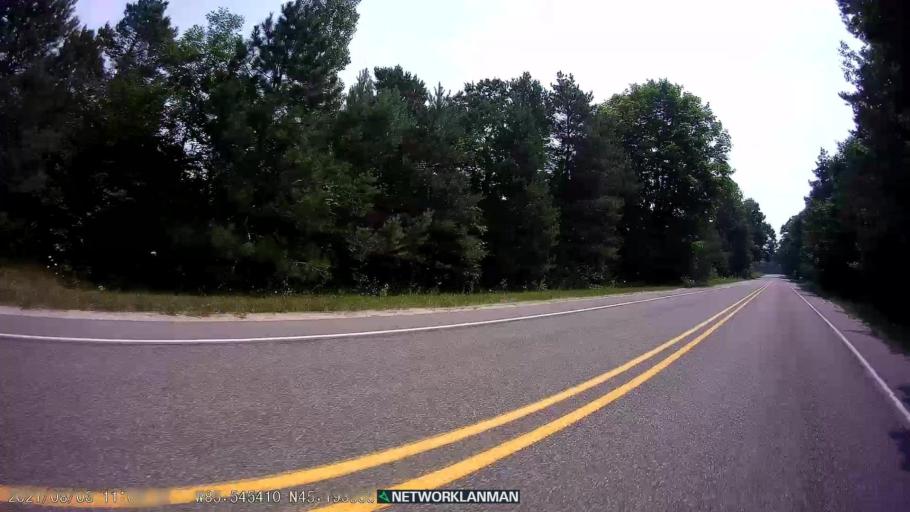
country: US
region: Michigan
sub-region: Leelanau County
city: Leland
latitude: 45.1933
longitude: -85.5455
